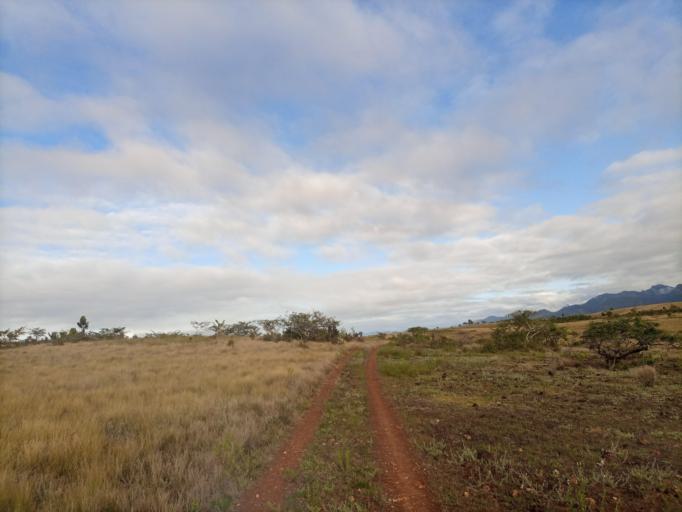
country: MG
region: Anosy
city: Fort Dauphin
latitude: -24.3147
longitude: 47.2590
